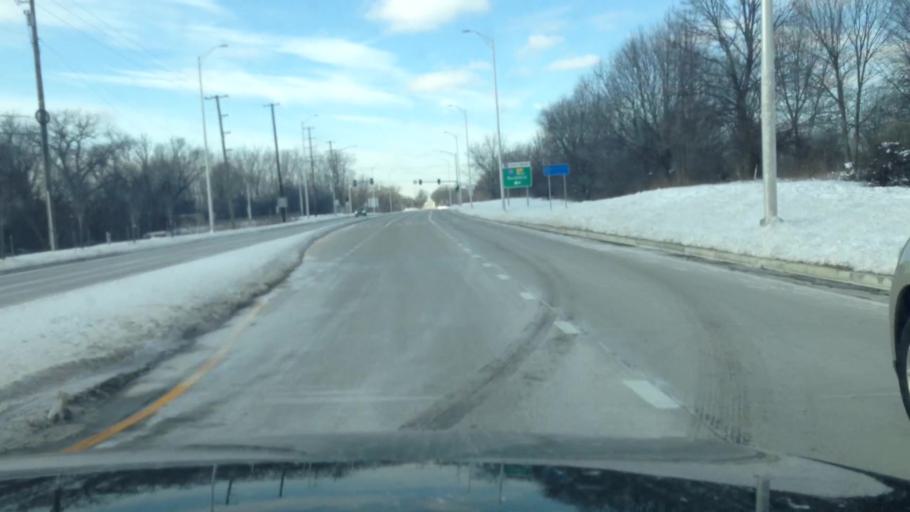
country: US
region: Illinois
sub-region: Cook County
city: Hoffman Estates
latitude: 42.0671
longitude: -88.0839
